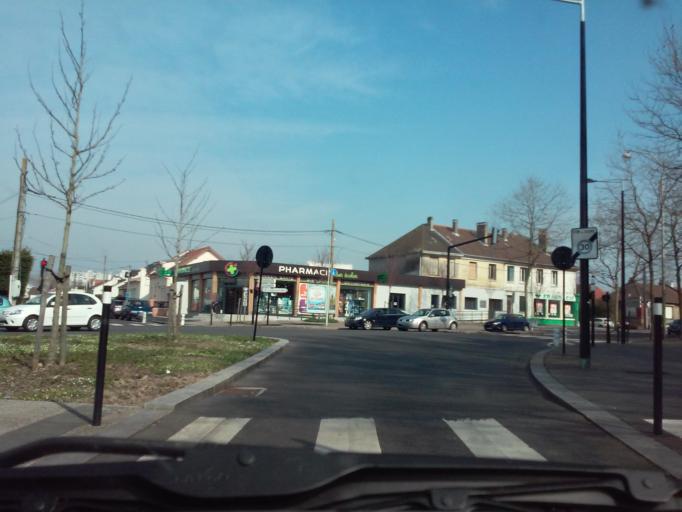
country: FR
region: Haute-Normandie
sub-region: Departement de la Seine-Maritime
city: Harfleur
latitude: 49.5094
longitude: 0.1662
